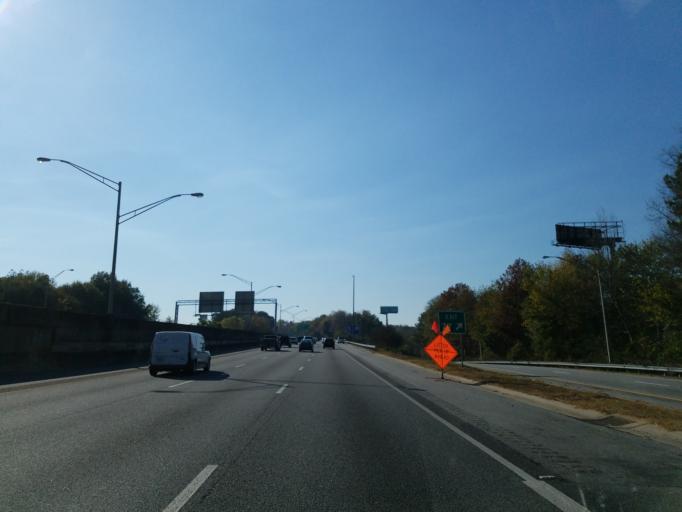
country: US
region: Georgia
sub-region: Fulton County
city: Hapeville
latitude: 33.6850
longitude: -84.4054
